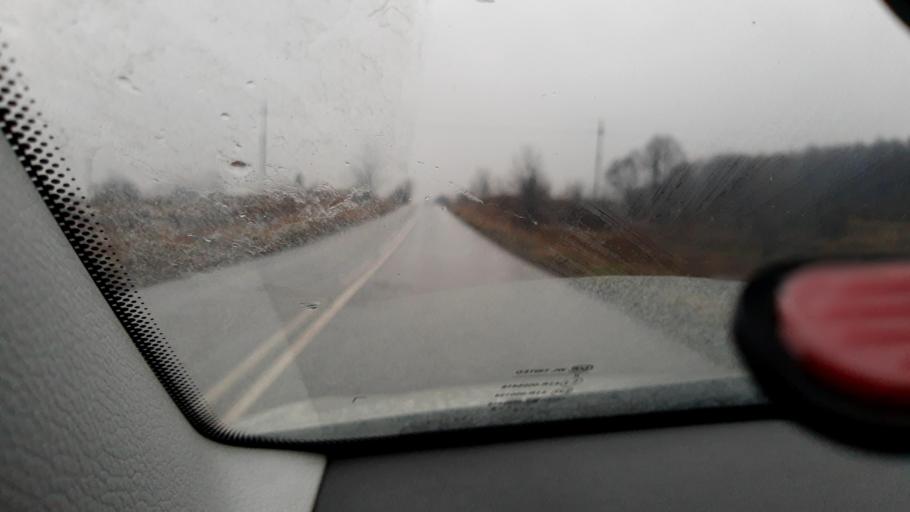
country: RU
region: Bashkortostan
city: Iglino
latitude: 54.9002
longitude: 56.2115
